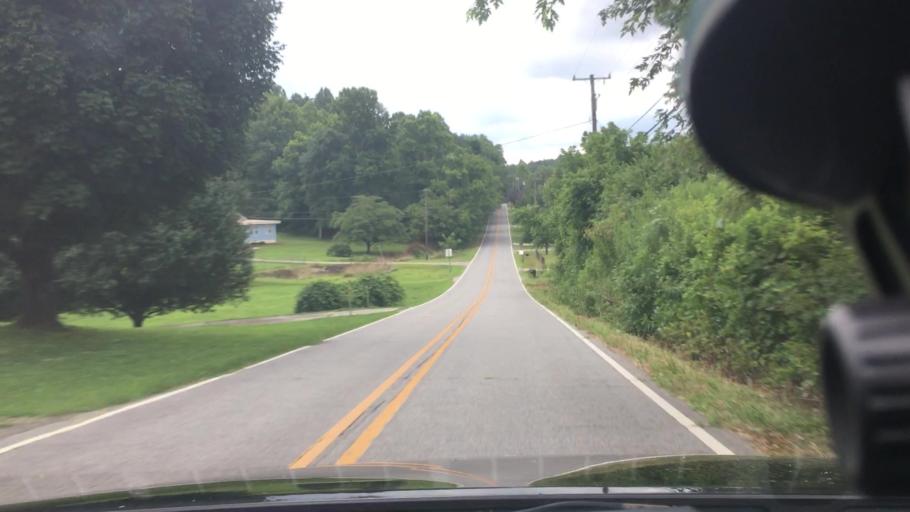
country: US
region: North Carolina
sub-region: McDowell County
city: West Marion
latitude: 35.6613
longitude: -82.0171
